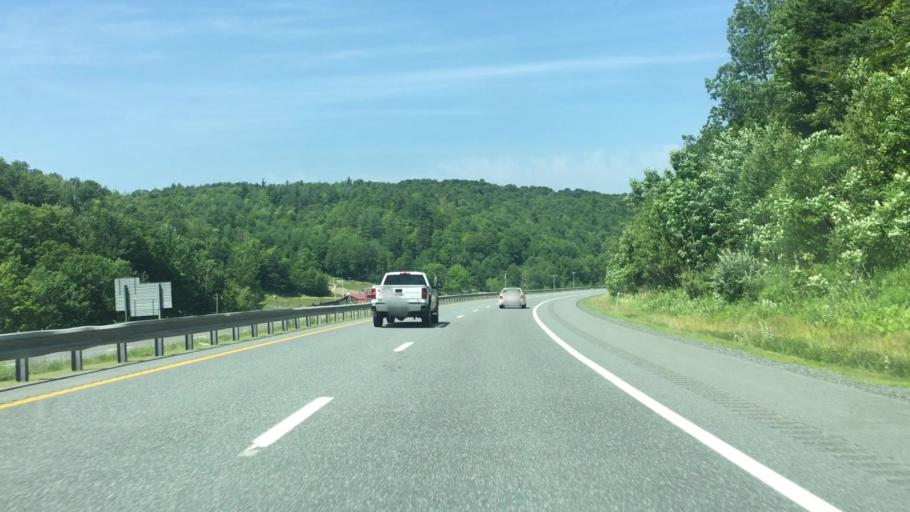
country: US
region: New Hampshire
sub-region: Grafton County
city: Enfield
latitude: 43.6018
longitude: -72.1771
